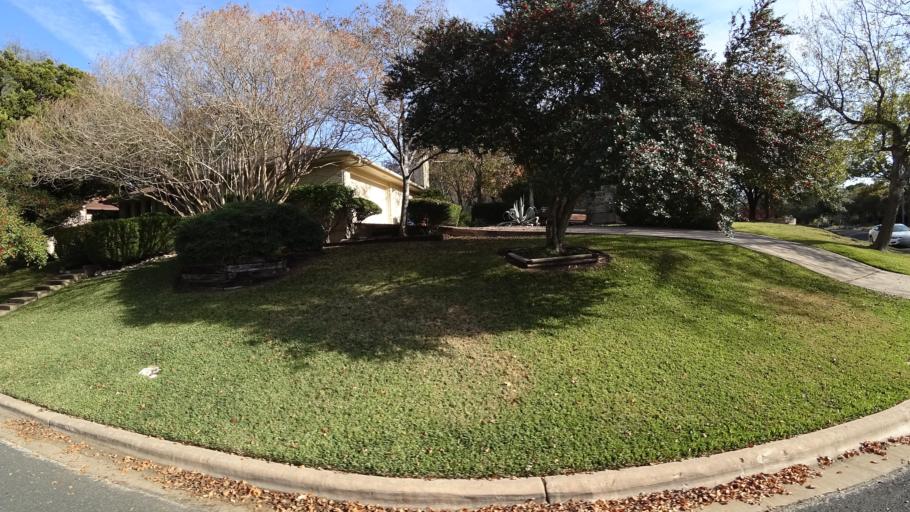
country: US
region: Texas
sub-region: Williamson County
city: Jollyville
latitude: 30.3856
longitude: -97.7577
